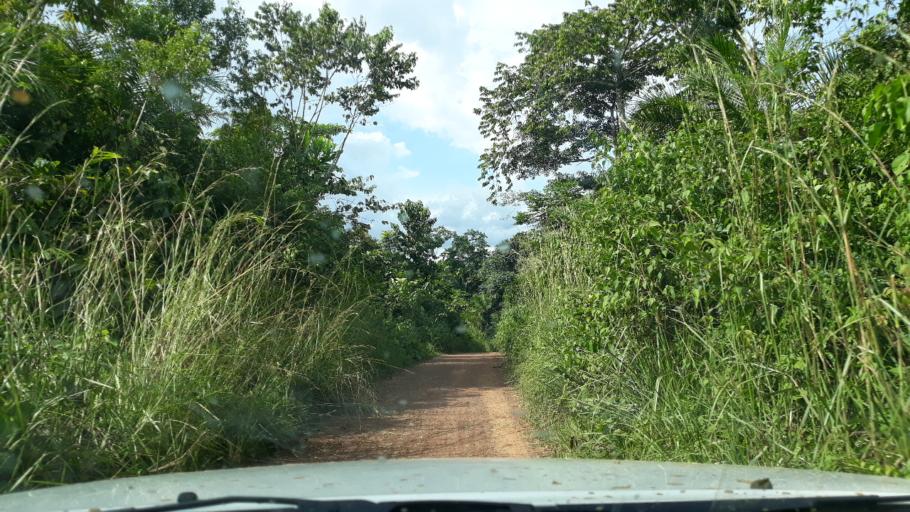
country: CD
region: Maniema
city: Kampene
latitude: -2.7577
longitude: 26.9274
